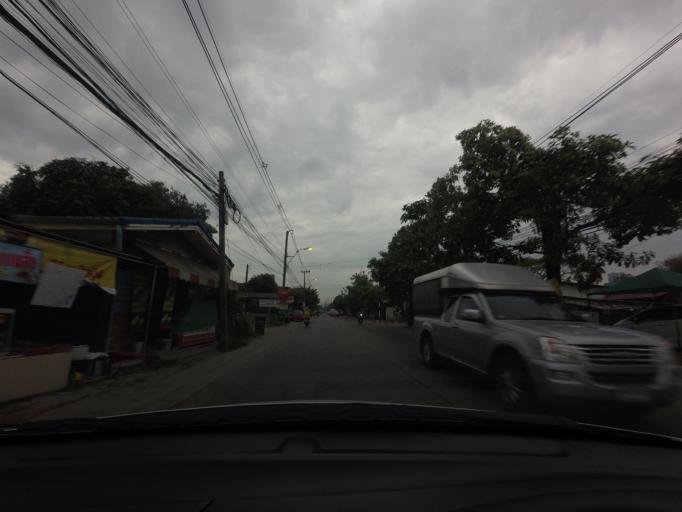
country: TH
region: Bangkok
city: Yan Nawa
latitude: 13.6777
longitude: 100.5604
